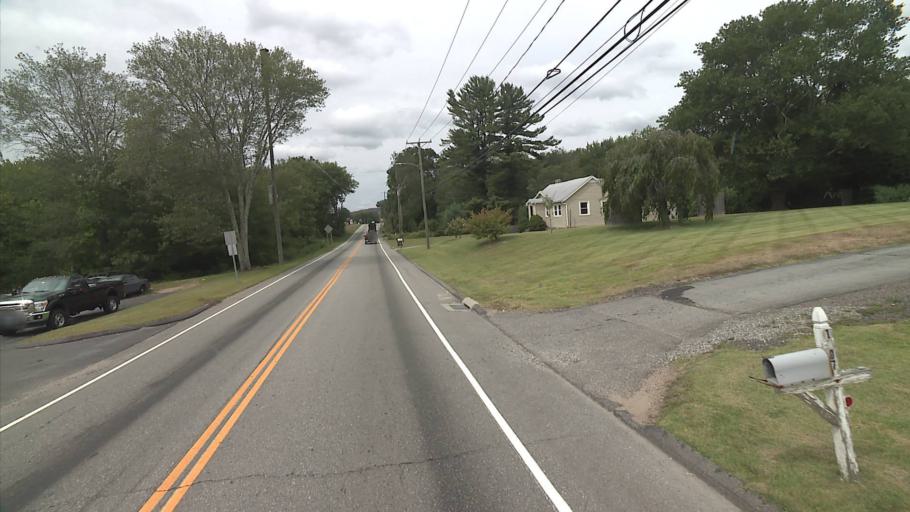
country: US
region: Connecticut
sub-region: New London County
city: Montville Center
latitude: 41.4298
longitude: -72.2179
